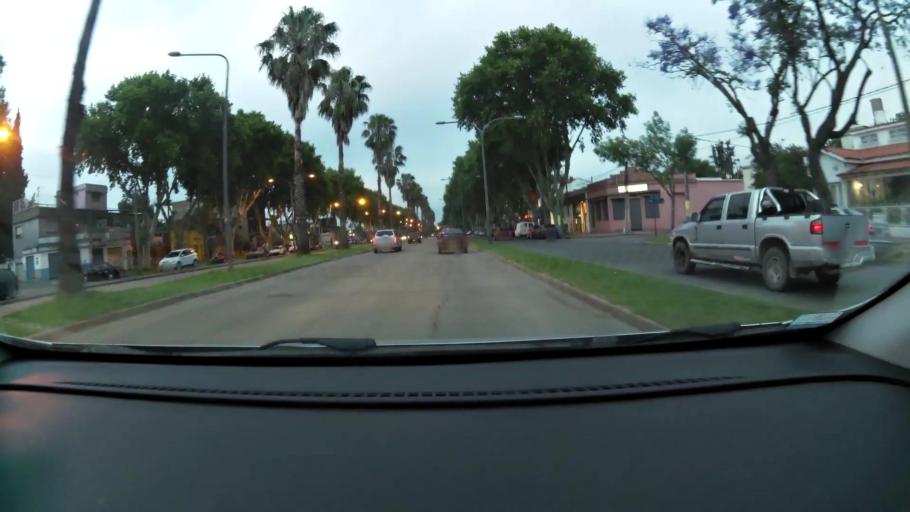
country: AR
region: Santa Fe
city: Granadero Baigorria
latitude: -32.8771
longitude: -60.6976
